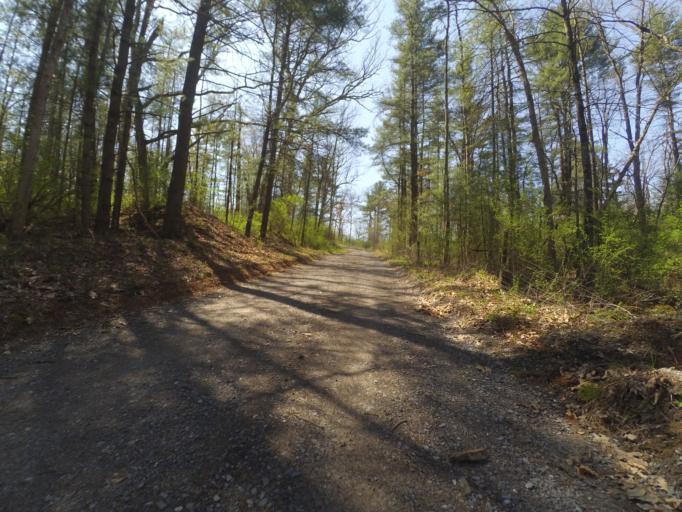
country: US
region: Pennsylvania
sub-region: Centre County
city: Houserville
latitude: 40.8334
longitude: -77.8484
